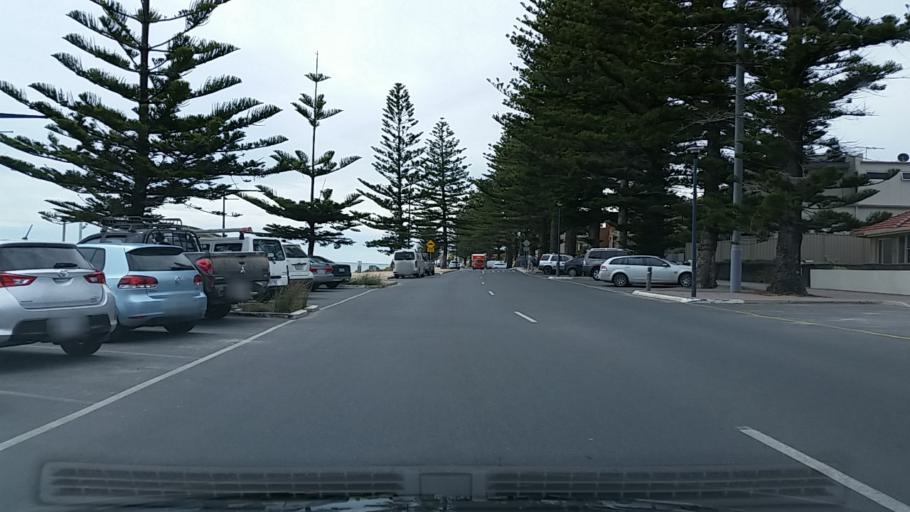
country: AU
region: South Australia
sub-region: Adelaide
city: Brighton
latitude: -35.0168
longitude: 138.5144
